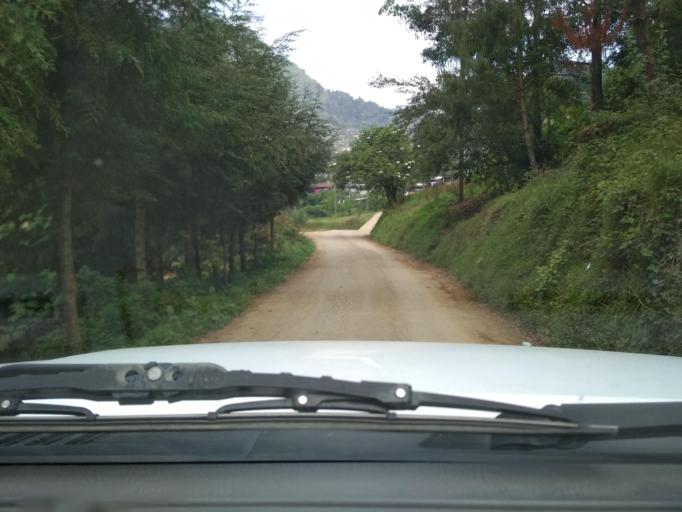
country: MX
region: Veracruz
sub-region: Camerino Z. Mendoza
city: Necoxtla
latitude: 18.7758
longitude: -97.1500
